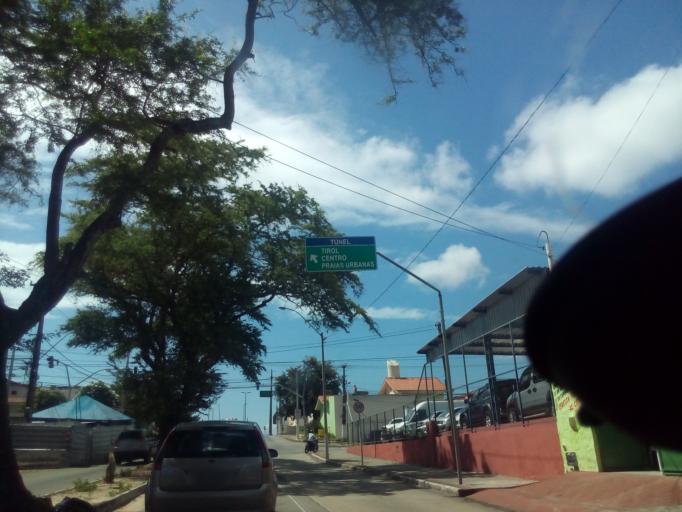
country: BR
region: Rio Grande do Norte
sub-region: Natal
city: Natal
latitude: -5.8267
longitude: -35.2184
